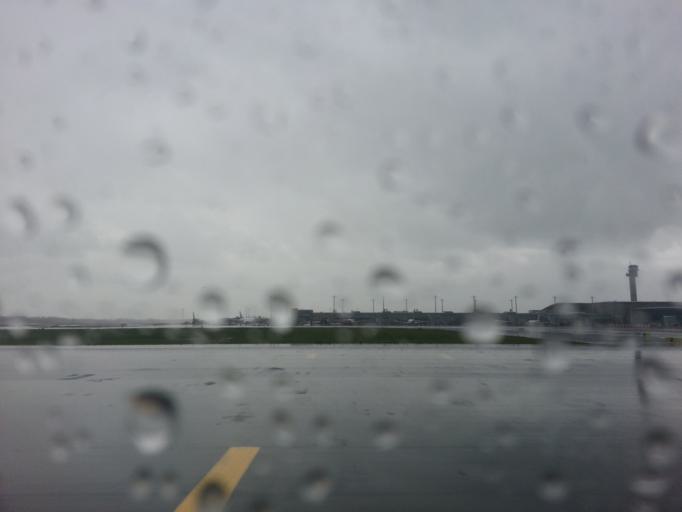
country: NO
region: Akershus
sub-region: Ullensaker
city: Jessheim
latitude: 60.1989
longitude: 11.1104
